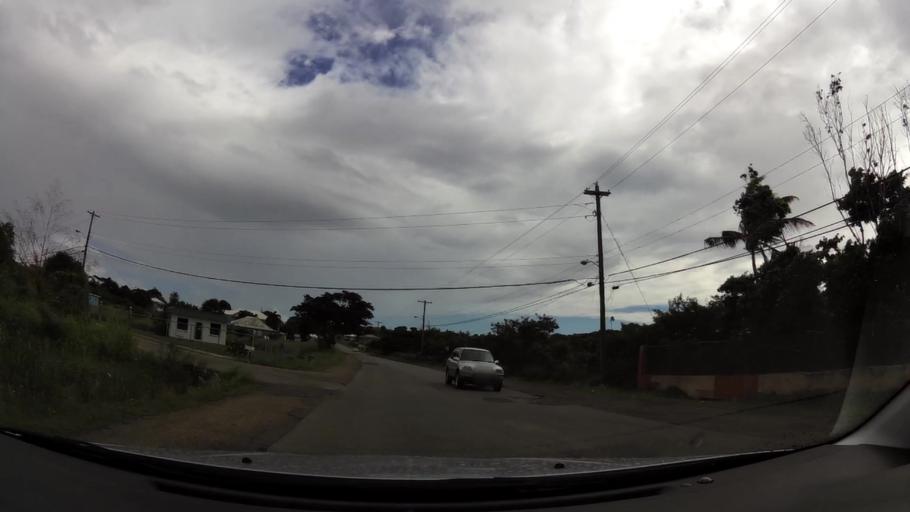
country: AG
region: Saint John
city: Potters Village
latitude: 17.1001
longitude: -61.8281
